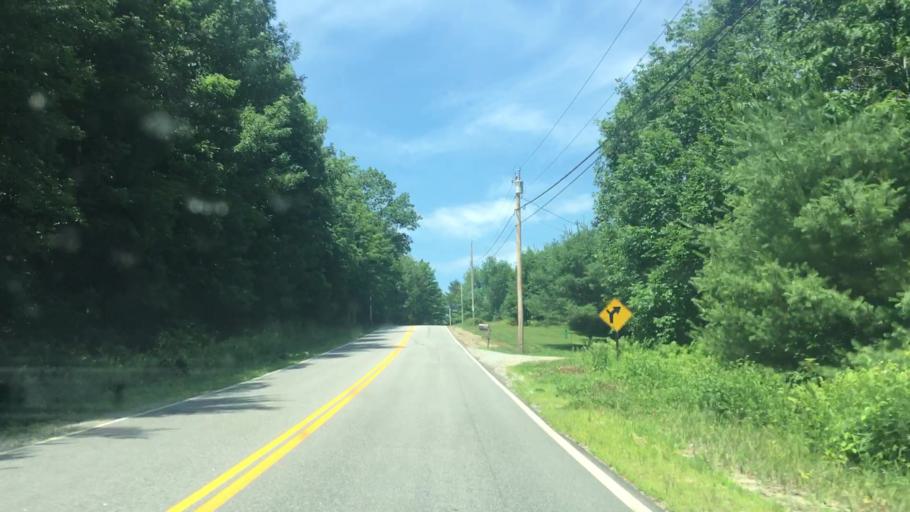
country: US
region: Maine
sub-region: Androscoggin County
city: Livermore
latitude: 44.3541
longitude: -70.2023
